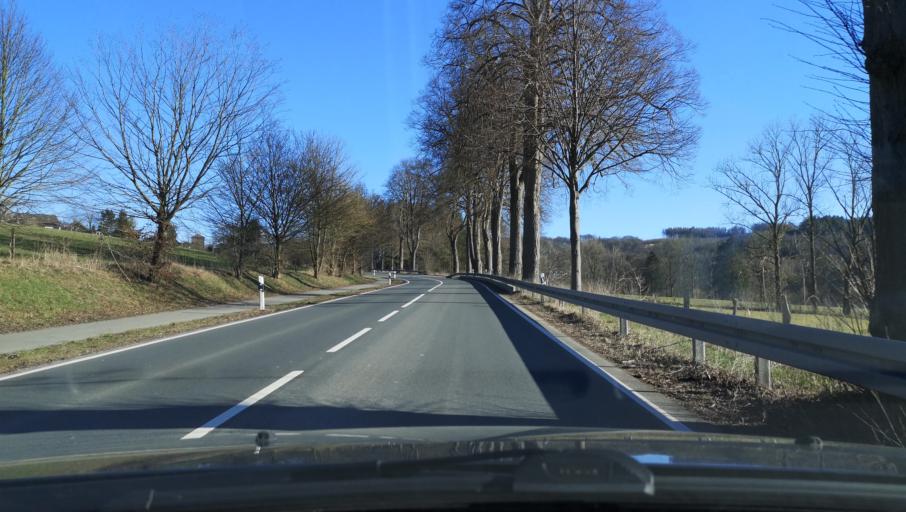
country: DE
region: North Rhine-Westphalia
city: Wipperfurth
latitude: 51.1143
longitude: 7.4640
